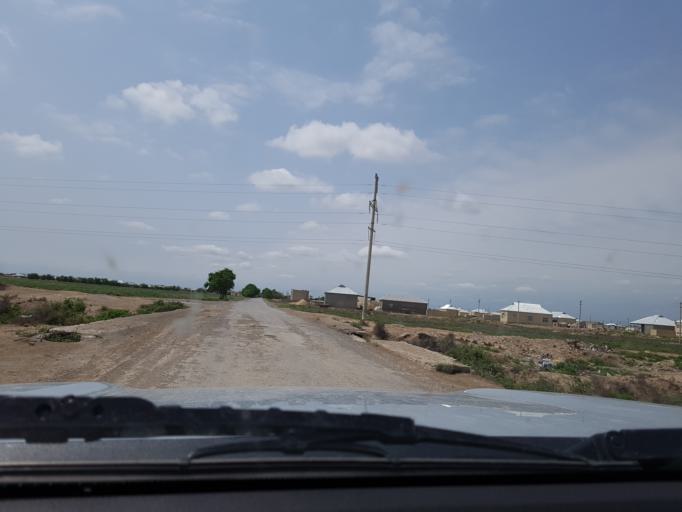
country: TM
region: Mary
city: Bayramaly
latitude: 37.6614
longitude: 62.1171
